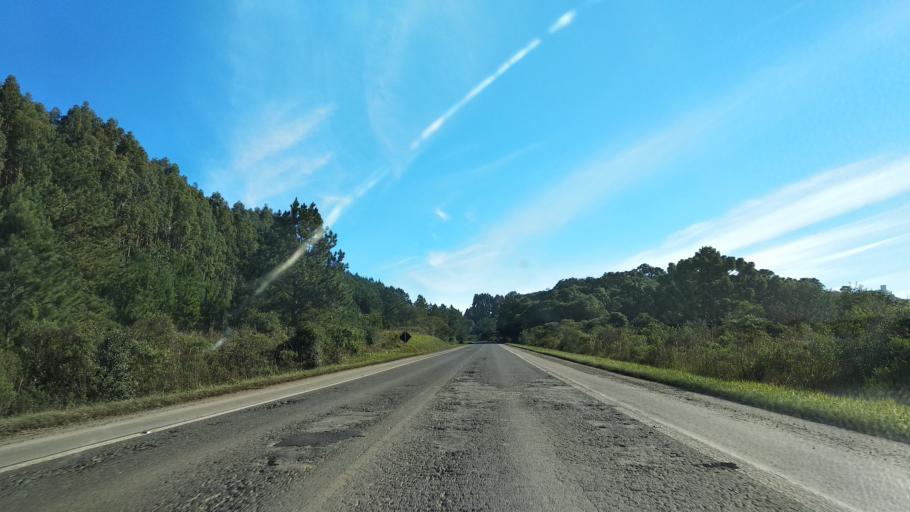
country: BR
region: Santa Catarina
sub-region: Campos Novos
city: Campos Novos
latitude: -27.3995
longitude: -51.1966
